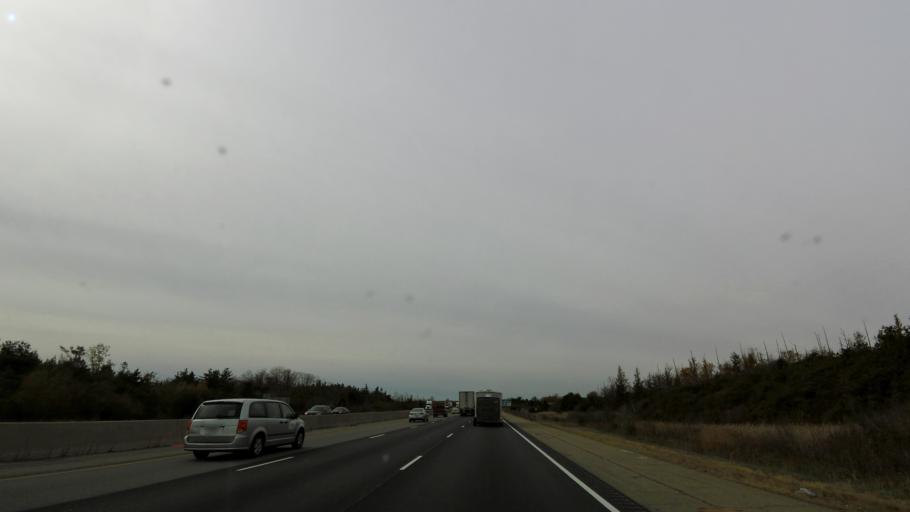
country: CA
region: Ontario
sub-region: Wellington County
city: Guelph
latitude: 43.4441
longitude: -80.1973
